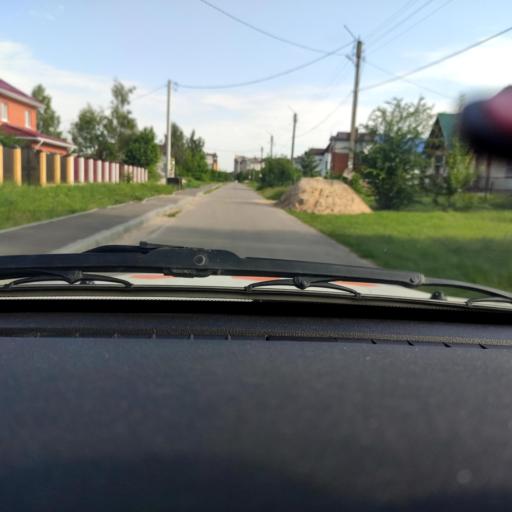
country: RU
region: Voronezj
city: Novaya Usman'
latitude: 51.6458
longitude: 39.3331
